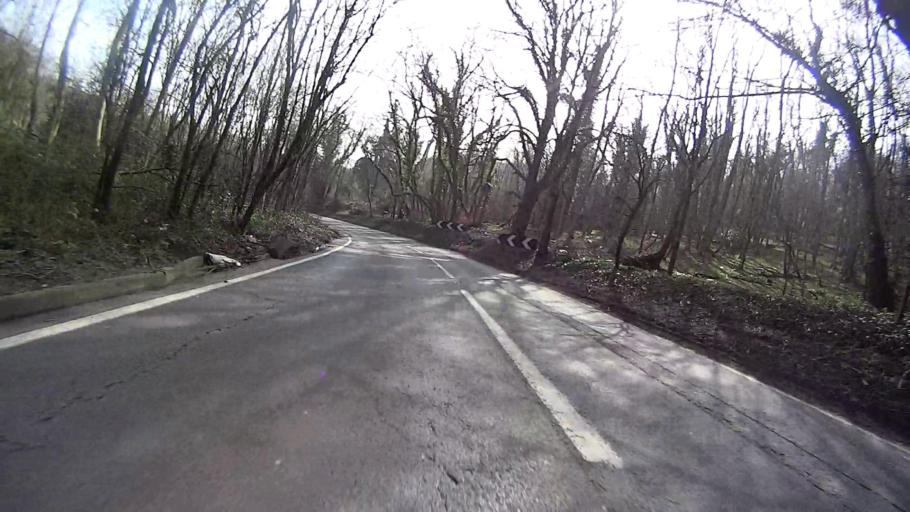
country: GB
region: England
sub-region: Surrey
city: Headley
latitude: 51.2610
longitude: -0.2643
